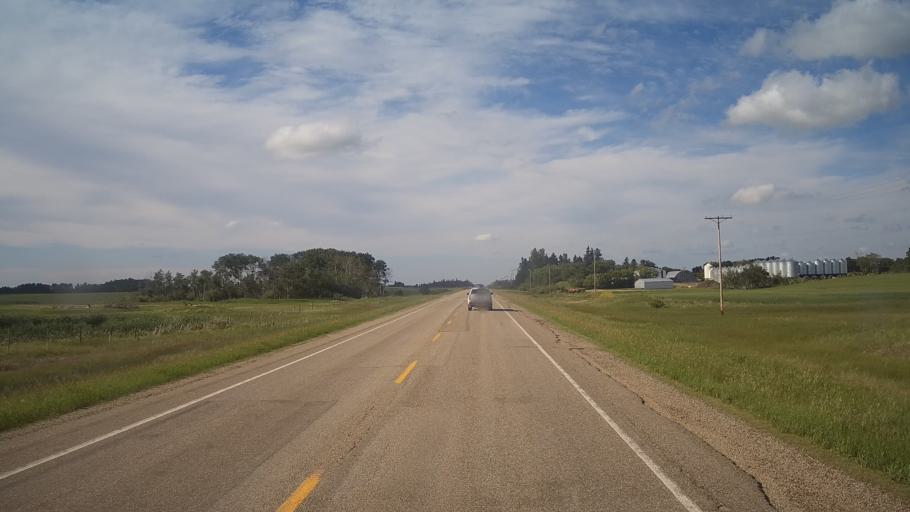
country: CA
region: Saskatchewan
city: Foam Lake
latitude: 51.5868
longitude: -103.8458
